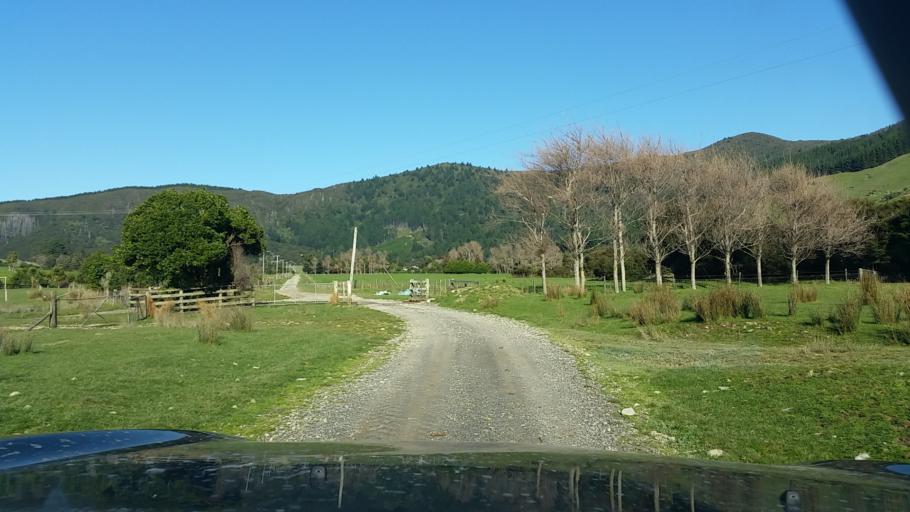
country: NZ
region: Marlborough
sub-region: Marlborough District
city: Picton
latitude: -41.1155
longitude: 174.0359
